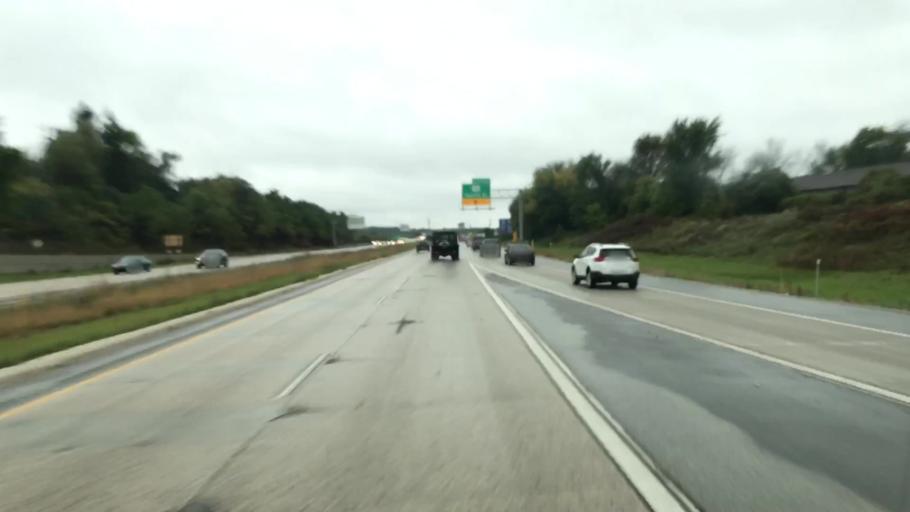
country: US
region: Wisconsin
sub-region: Waukesha County
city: Pewaukee
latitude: 43.0745
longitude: -88.2513
